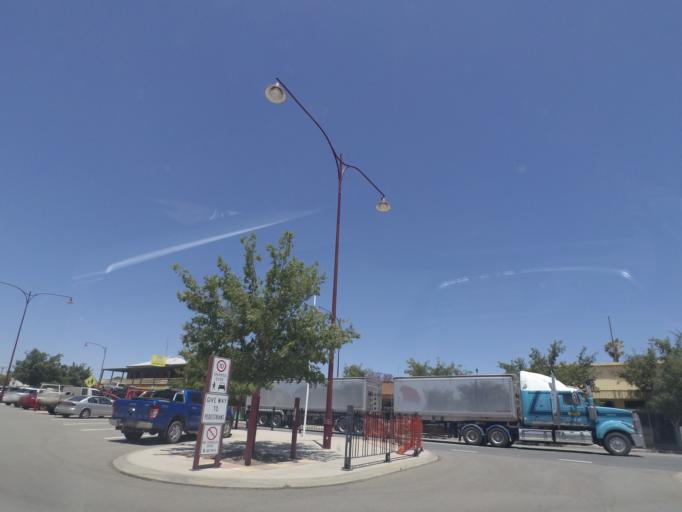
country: AU
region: New South Wales
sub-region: Berrigan
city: Berrigan
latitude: -35.3559
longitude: 145.7279
